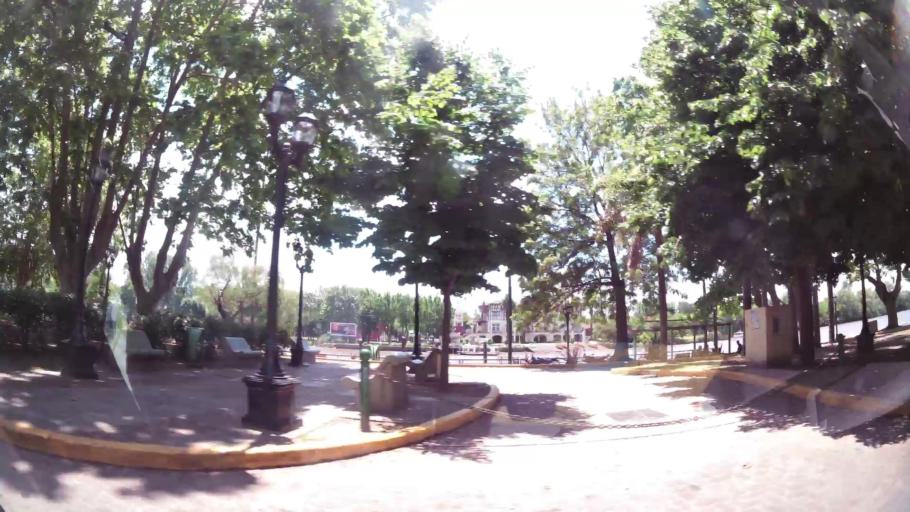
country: AR
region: Buenos Aires
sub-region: Partido de Tigre
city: Tigre
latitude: -34.4154
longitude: -58.5807
